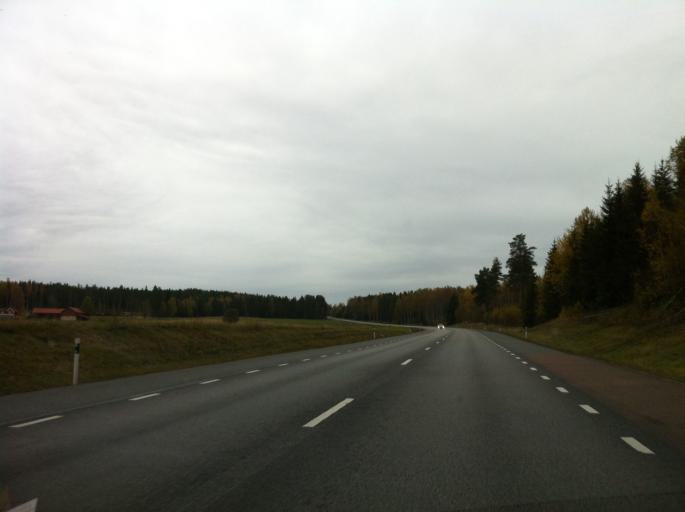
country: SE
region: OErebro
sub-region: Lindesbergs Kommun
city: Stora
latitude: 59.7622
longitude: 15.1476
